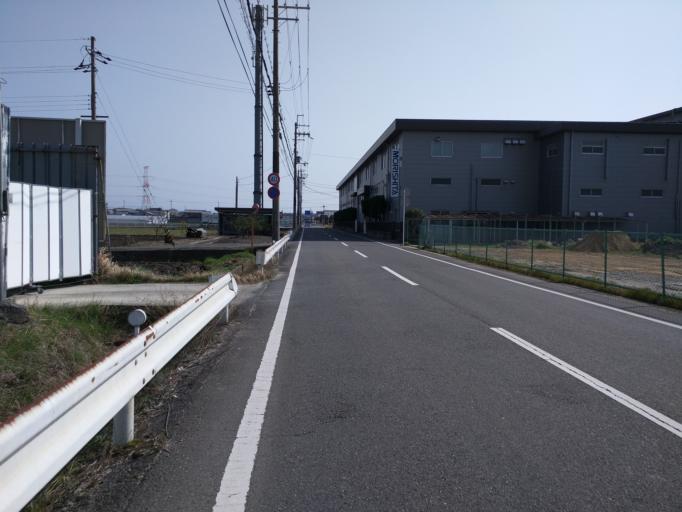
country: JP
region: Kyoto
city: Tanabe
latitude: 34.7660
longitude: 135.7974
